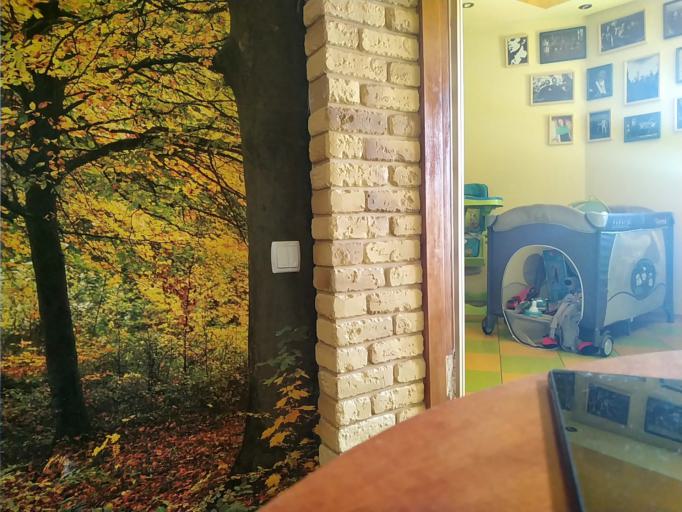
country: RU
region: Tverskaya
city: Vyshniy Volochek
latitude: 57.5890
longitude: 34.5650
